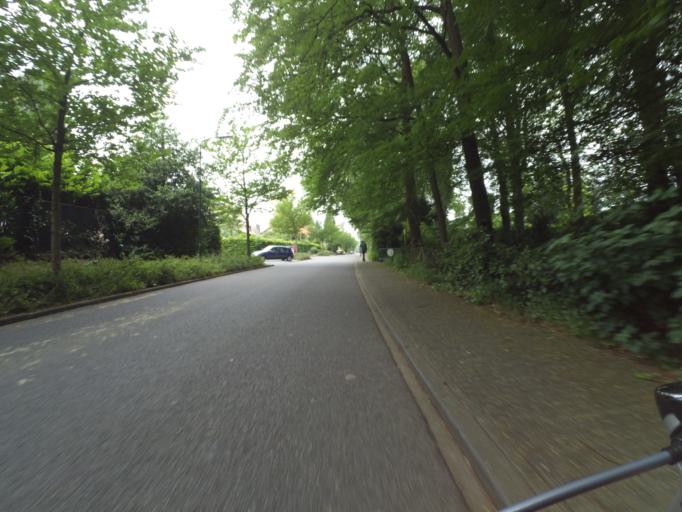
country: NL
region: Gelderland
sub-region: Gemeente Renkum
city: Oosterbeek
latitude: 51.9846
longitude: 5.8225
